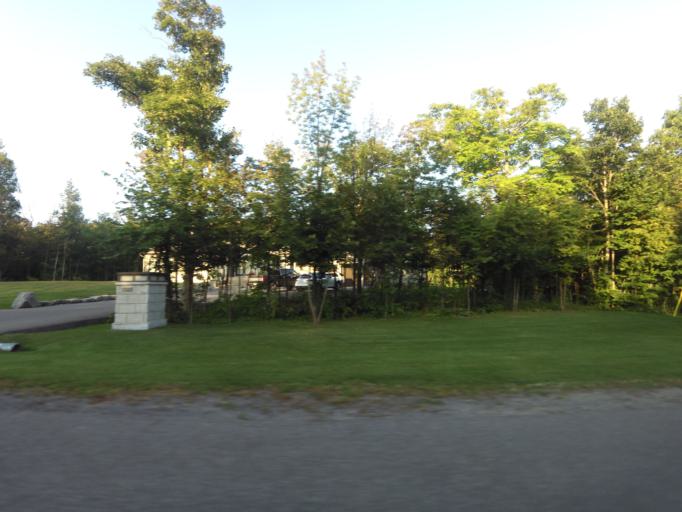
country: CA
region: Ontario
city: Clarence-Rockland
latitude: 45.5043
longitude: -75.4252
